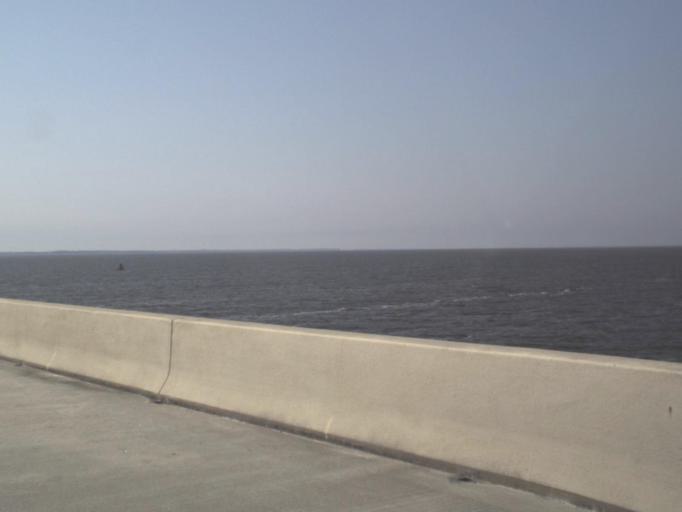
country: US
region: Florida
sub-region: Franklin County
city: Eastpoint
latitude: 29.7034
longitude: -84.8905
